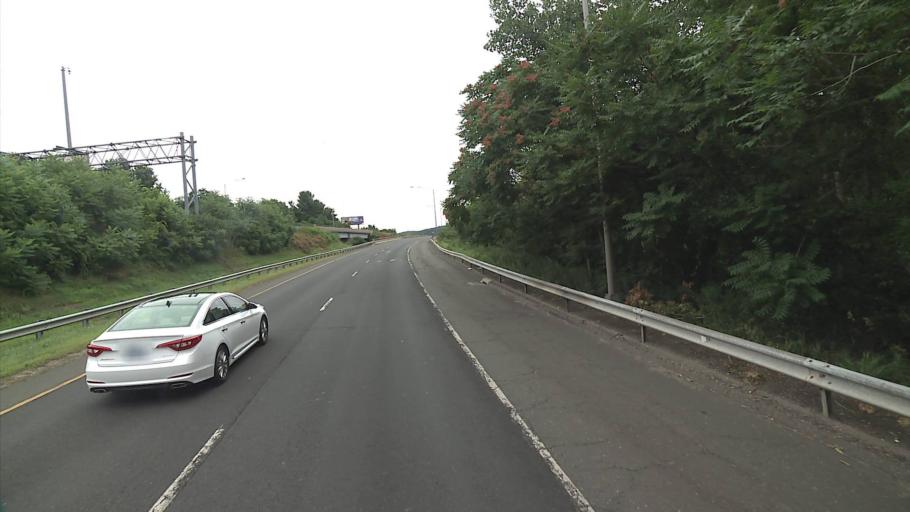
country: US
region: Connecticut
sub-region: New Haven County
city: Waterbury
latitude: 41.5674
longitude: -73.0574
